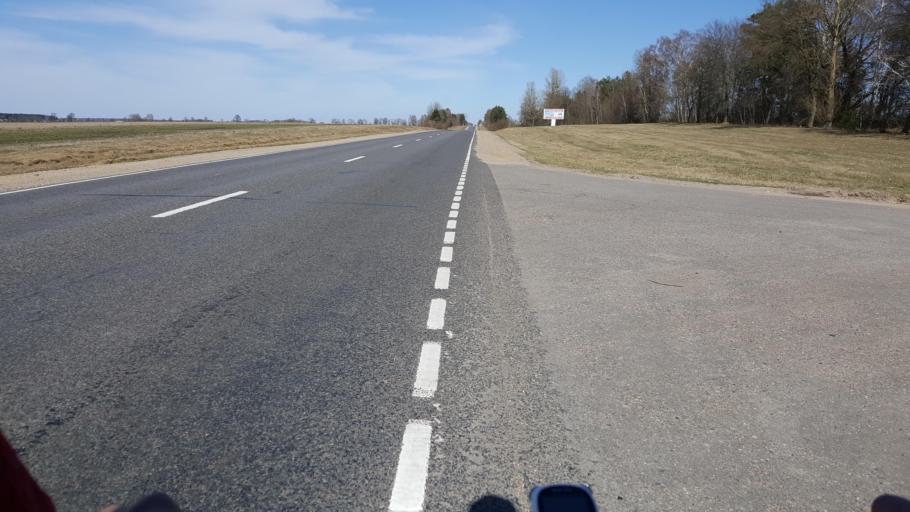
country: BY
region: Brest
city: Kamyanyets
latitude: 52.3597
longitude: 23.7780
